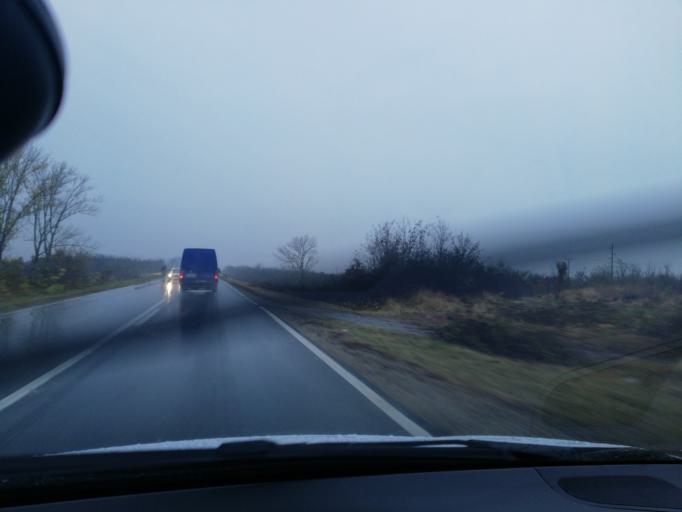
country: RS
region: Autonomna Pokrajina Vojvodina
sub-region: Sremski Okrug
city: Ruma
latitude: 45.0217
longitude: 19.8369
